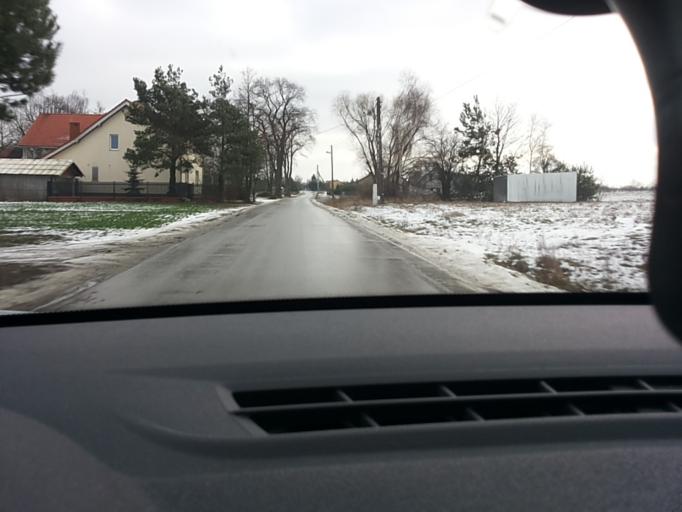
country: PL
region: Lodz Voivodeship
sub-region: Powiat skierniewicki
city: Makow
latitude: 51.9861
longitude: 20.0934
